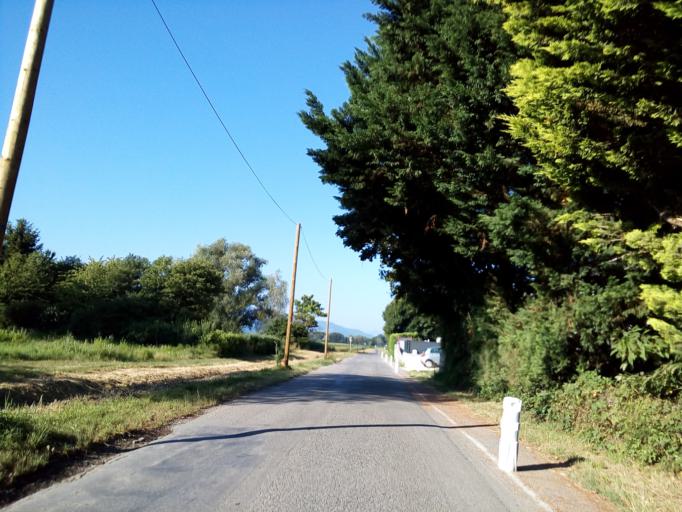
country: FR
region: Rhone-Alpes
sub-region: Departement de l'Isere
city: Lumbin
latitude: 45.3034
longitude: 5.9144
